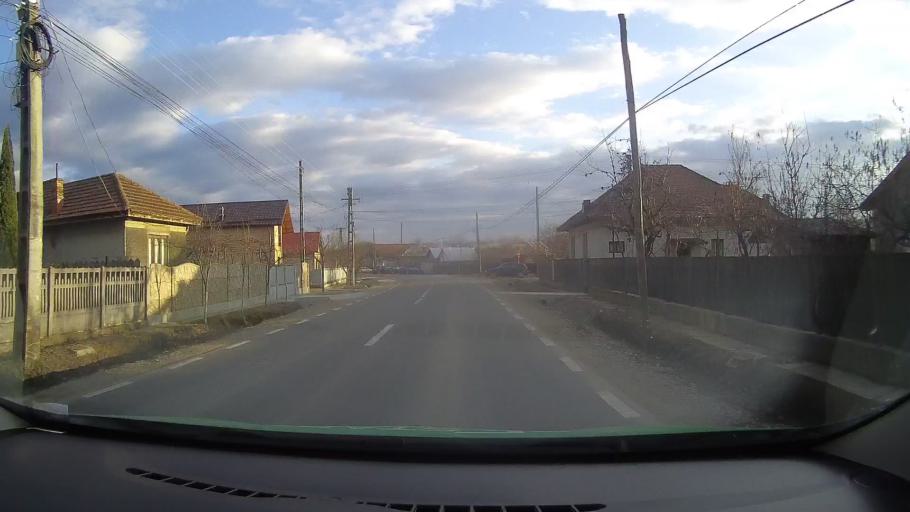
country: RO
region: Dambovita
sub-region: Comuna I. L. Caragiale
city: Ghirdoveni
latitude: 44.9506
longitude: 25.6583
